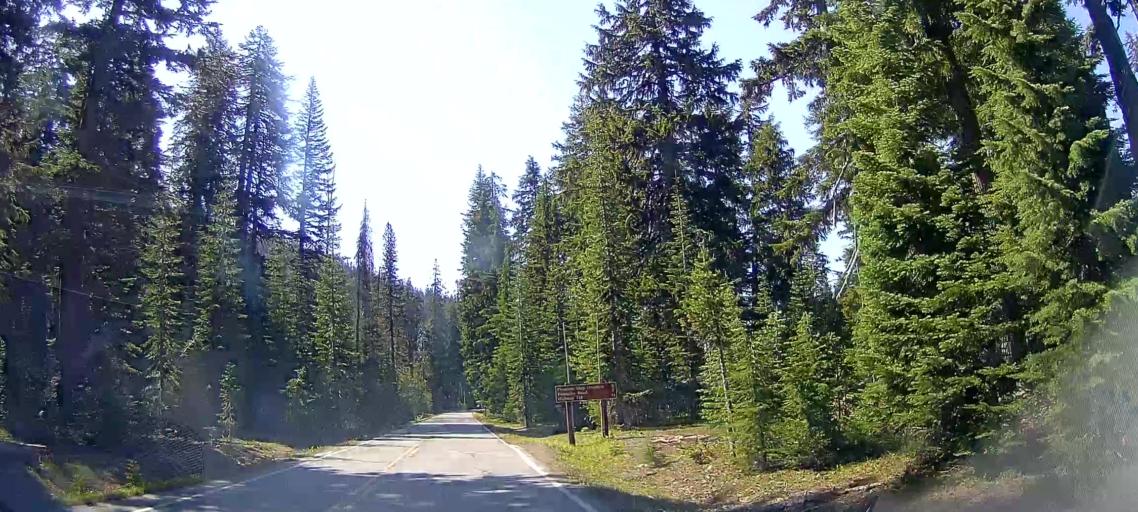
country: US
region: Oregon
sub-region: Jackson County
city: Shady Cove
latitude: 42.8934
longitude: -122.1342
